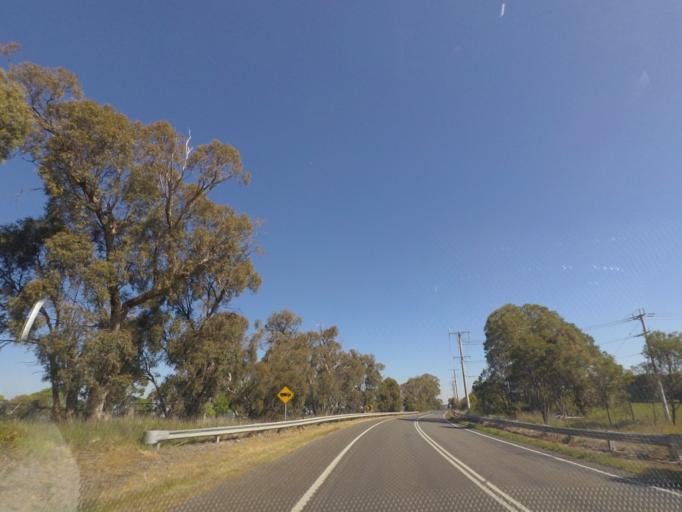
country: AU
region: Victoria
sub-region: Whittlesea
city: Whittlesea
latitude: -37.3298
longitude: 144.9839
